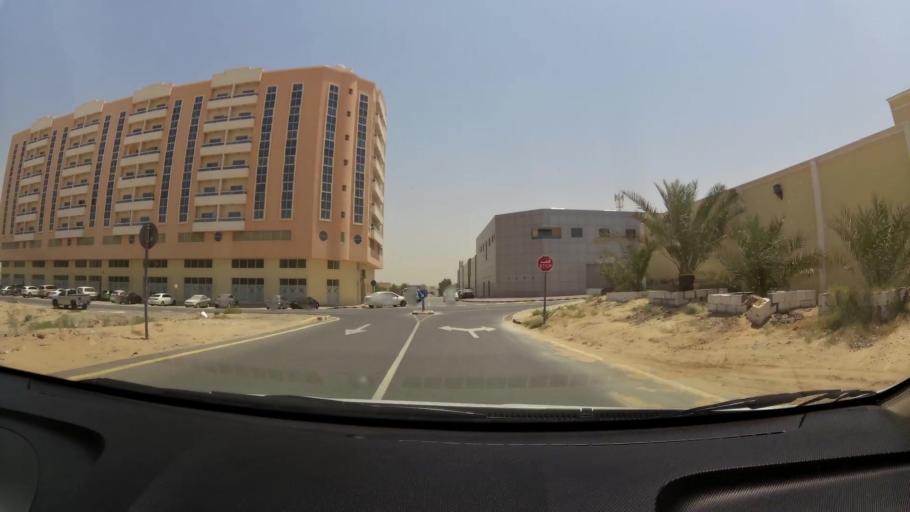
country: AE
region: Ajman
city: Ajman
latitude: 25.4098
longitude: 55.5159
